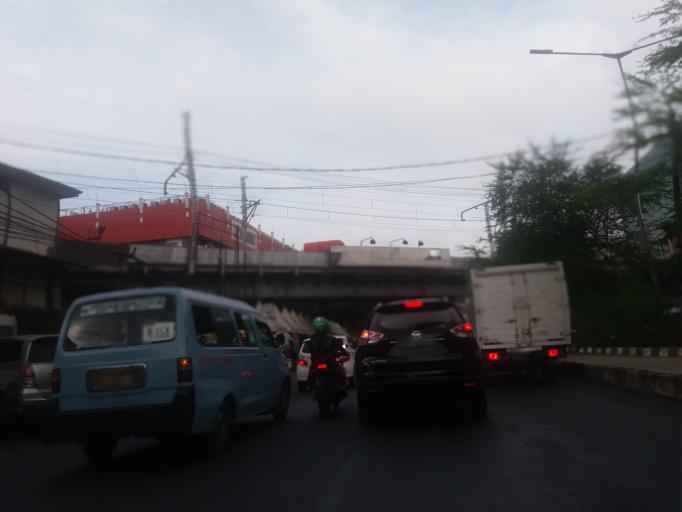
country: ID
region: Jakarta Raya
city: Jakarta
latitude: -6.1369
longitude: 106.8208
